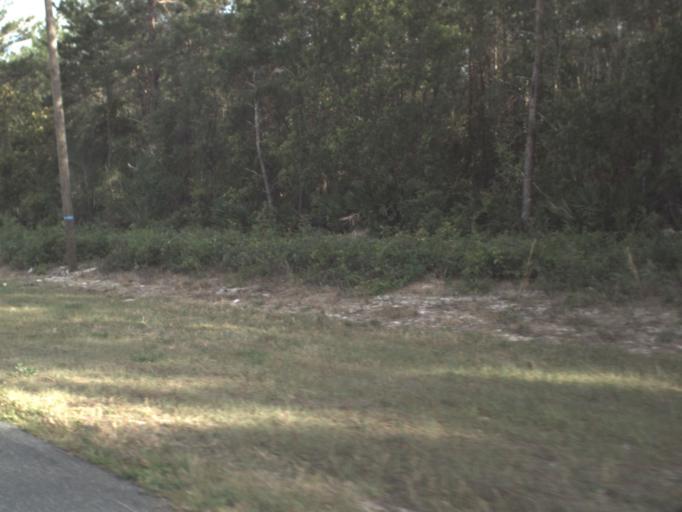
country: US
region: Florida
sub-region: Lake County
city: Astor
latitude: 29.1568
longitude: -81.5806
